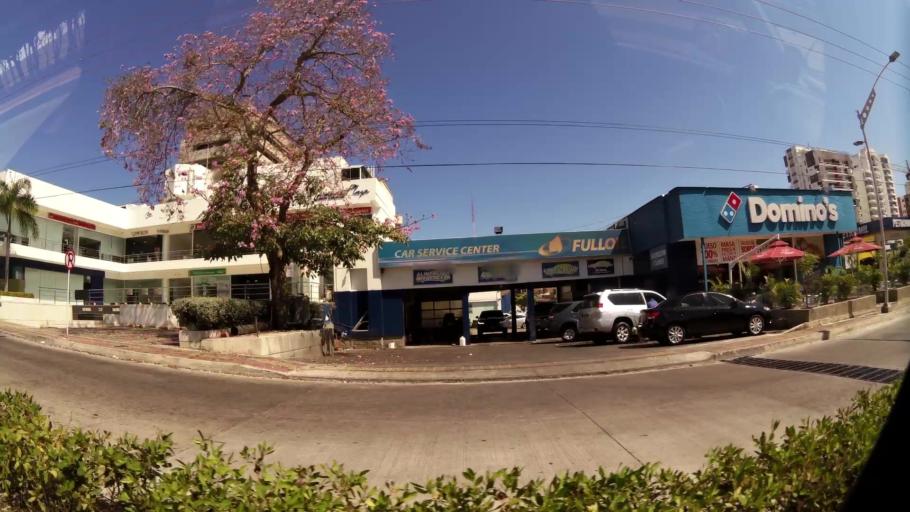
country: CO
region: Atlantico
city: Barranquilla
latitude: 11.0060
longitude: -74.8178
